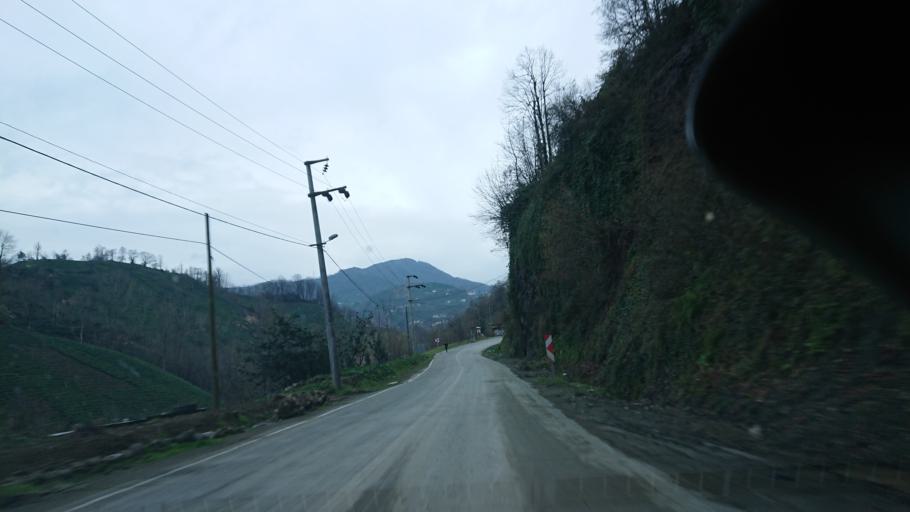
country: TR
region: Rize
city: Rize
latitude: 41.0161
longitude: 40.4959
